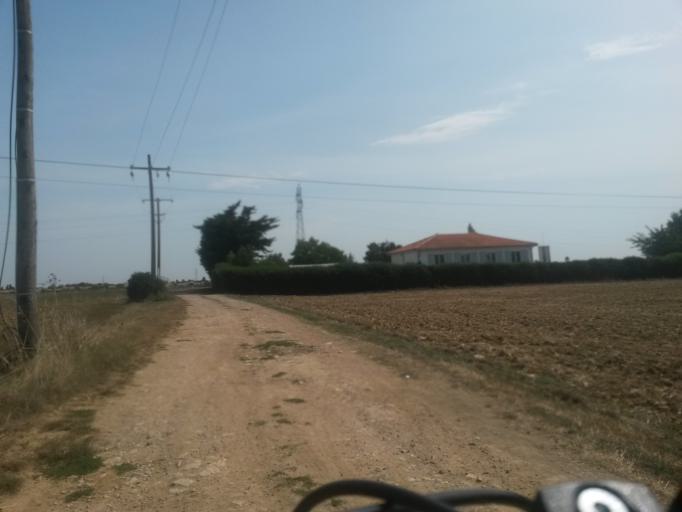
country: FR
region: Poitou-Charentes
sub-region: Departement de la Charente-Maritime
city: Puilboreau
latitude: 46.2015
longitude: -1.1210
